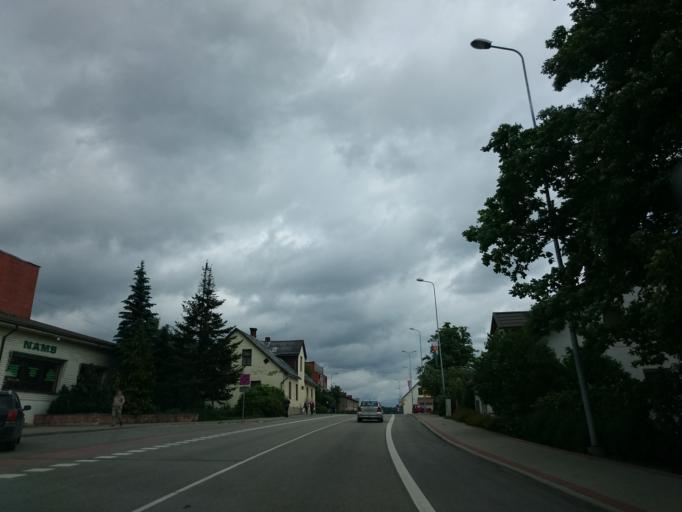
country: LV
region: Madonas Rajons
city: Madona
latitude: 56.8567
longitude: 26.2249
